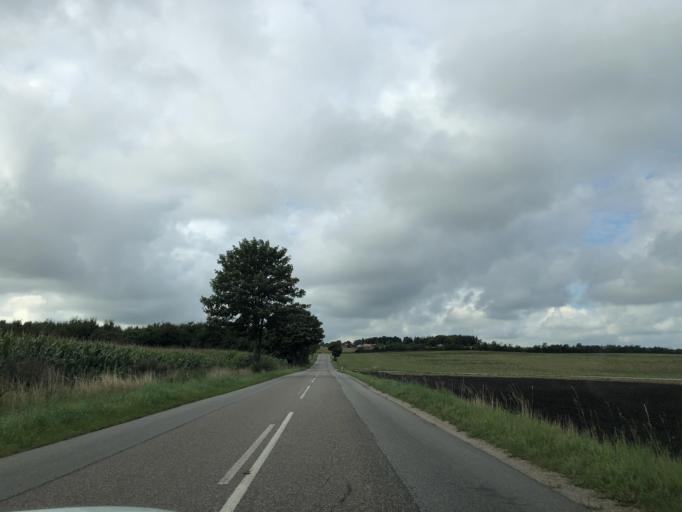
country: DK
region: North Denmark
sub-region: Alborg Kommune
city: Frejlev
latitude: 56.9395
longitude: 9.7710
